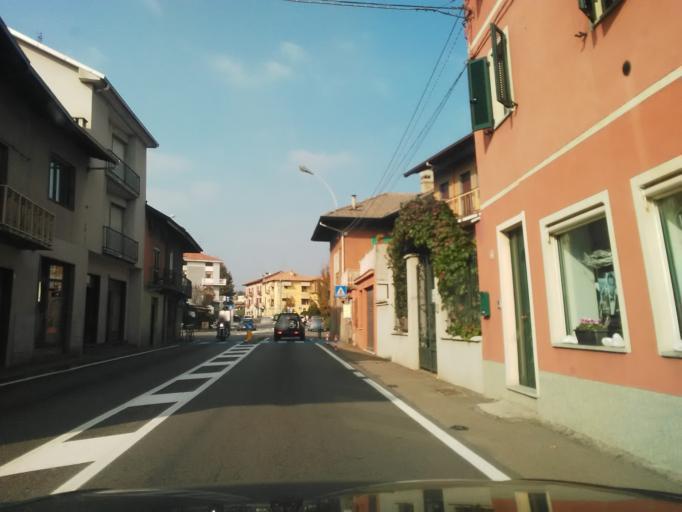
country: IT
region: Piedmont
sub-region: Provincia di Biella
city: Gaglianico
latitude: 45.5381
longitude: 8.0736
